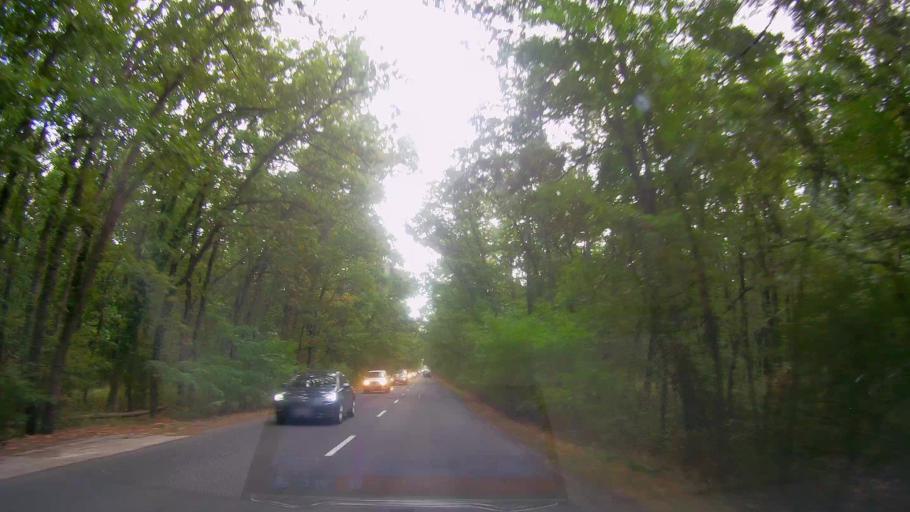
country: BG
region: Burgas
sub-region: Obshtina Primorsko
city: Primorsko
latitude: 42.2808
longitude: 27.7384
